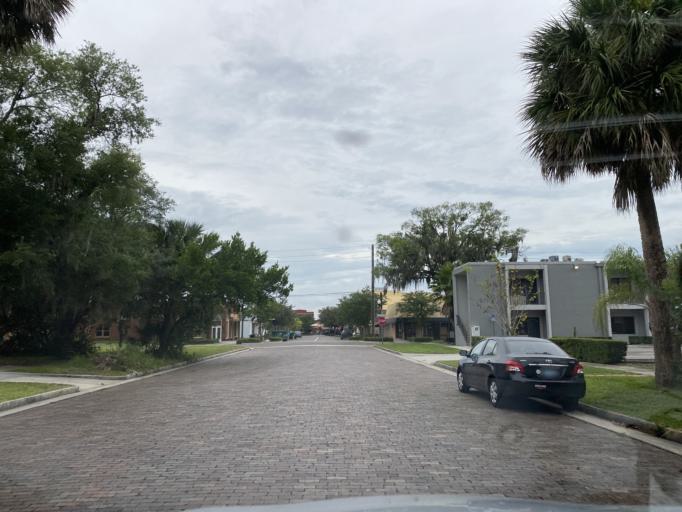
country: US
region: Florida
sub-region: Seminole County
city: Sanford
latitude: 28.8093
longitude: -81.2670
